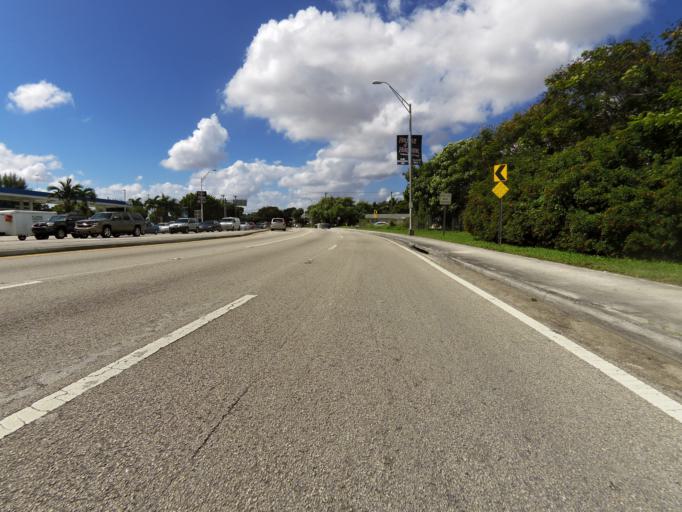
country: US
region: Florida
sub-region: Miami-Dade County
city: Westwood Lake
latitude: 25.7321
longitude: -80.3865
